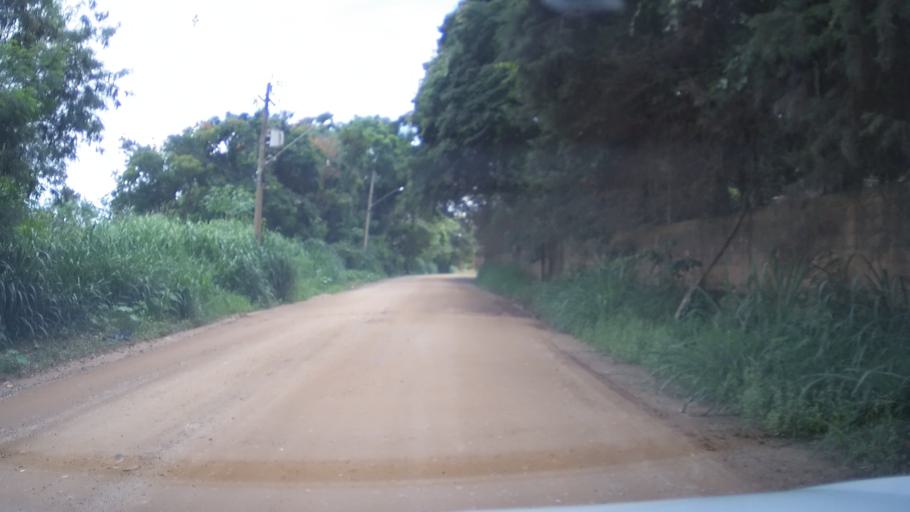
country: BR
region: Sao Paulo
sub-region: Valinhos
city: Valinhos
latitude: -22.9927
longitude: -46.9887
